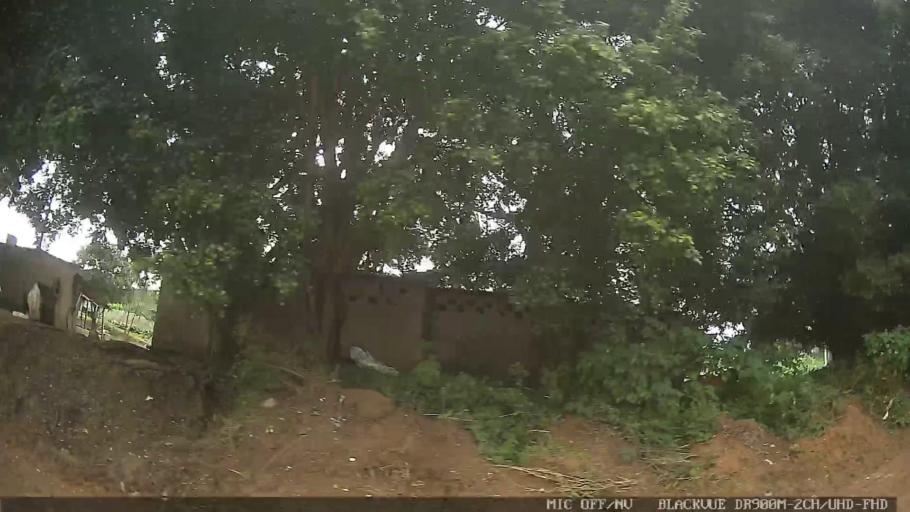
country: BR
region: Sao Paulo
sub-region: Itaquaquecetuba
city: Itaquaquecetuba
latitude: -23.4587
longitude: -46.3035
